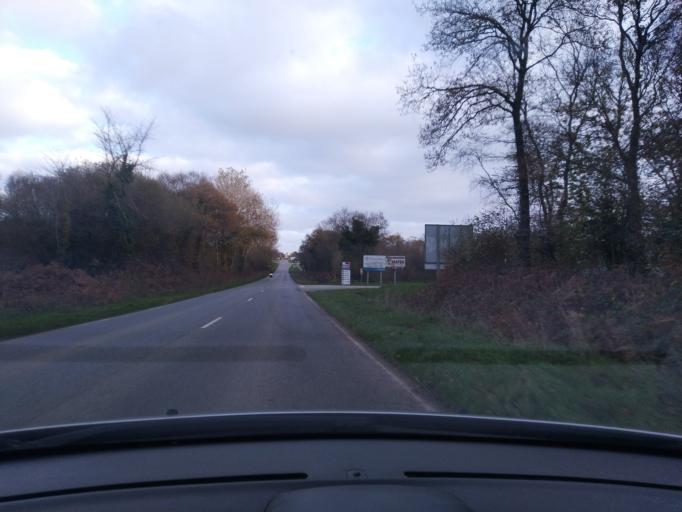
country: FR
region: Brittany
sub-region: Departement du Finistere
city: Plouigneau
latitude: 48.5720
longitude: -3.7284
